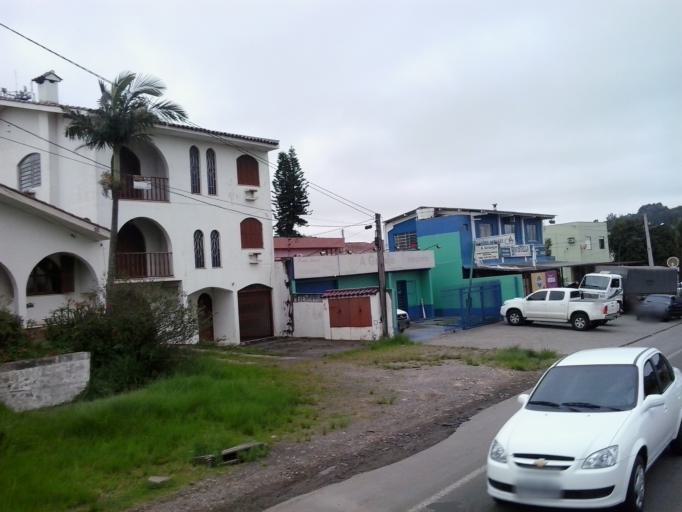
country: BR
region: Rio Grande do Sul
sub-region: Santa Maria
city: Santa Maria
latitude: -29.6953
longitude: -53.7657
